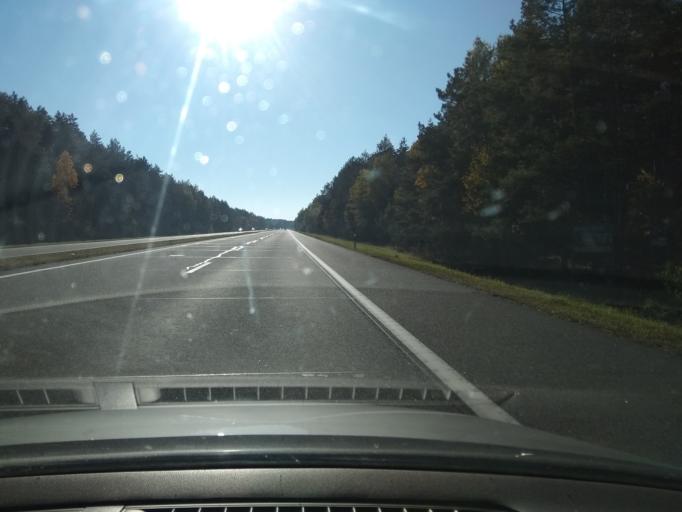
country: BY
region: Brest
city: Baranovichi
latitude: 53.0652
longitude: 25.8740
